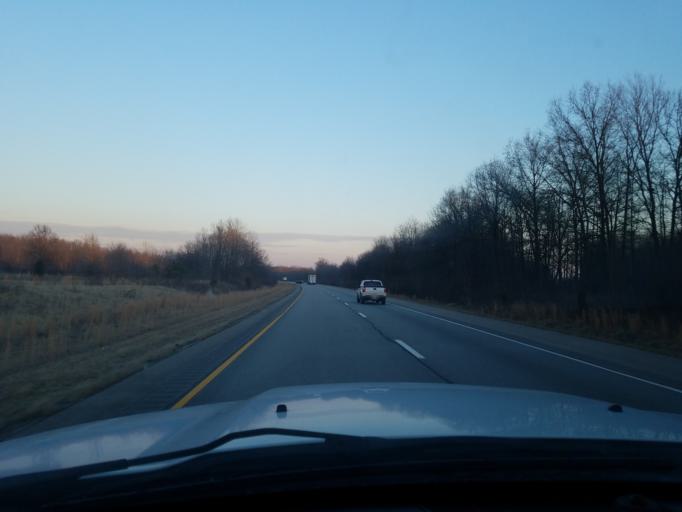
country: US
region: Indiana
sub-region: Warrick County
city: Chandler
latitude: 38.1833
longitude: -87.3739
